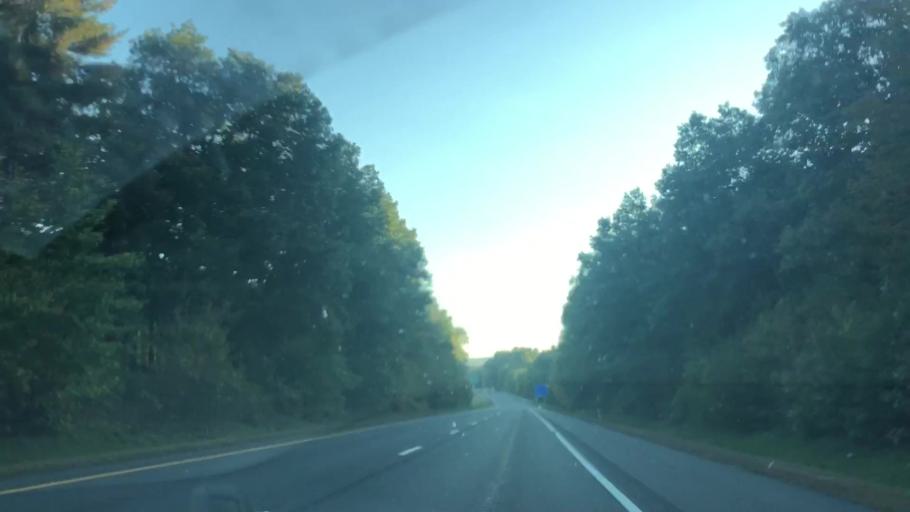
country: US
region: Massachusetts
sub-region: Franklin County
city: Turners Falls
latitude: 42.6364
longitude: -72.5762
